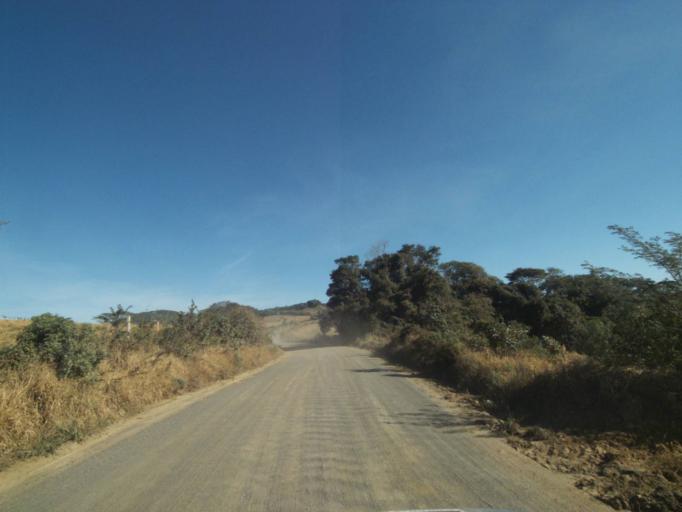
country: BR
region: Parana
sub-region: Tibagi
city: Tibagi
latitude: -24.5350
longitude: -50.4632
